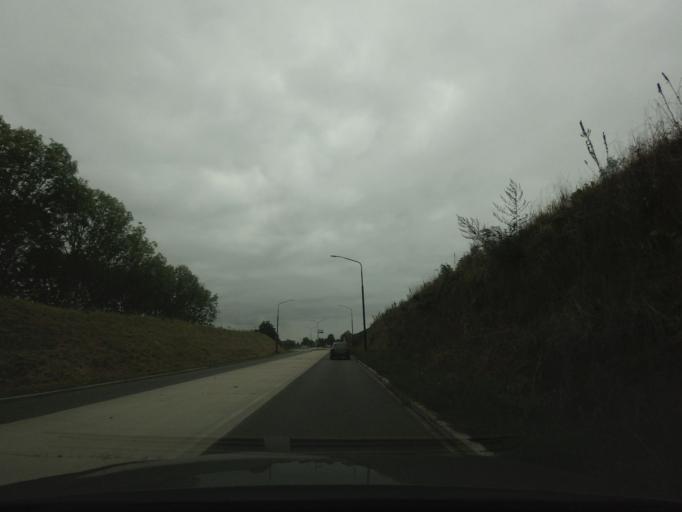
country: NL
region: North Holland
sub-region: Gemeente Heerhugowaard
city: Heerhugowaard
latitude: 52.6580
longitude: 4.8416
